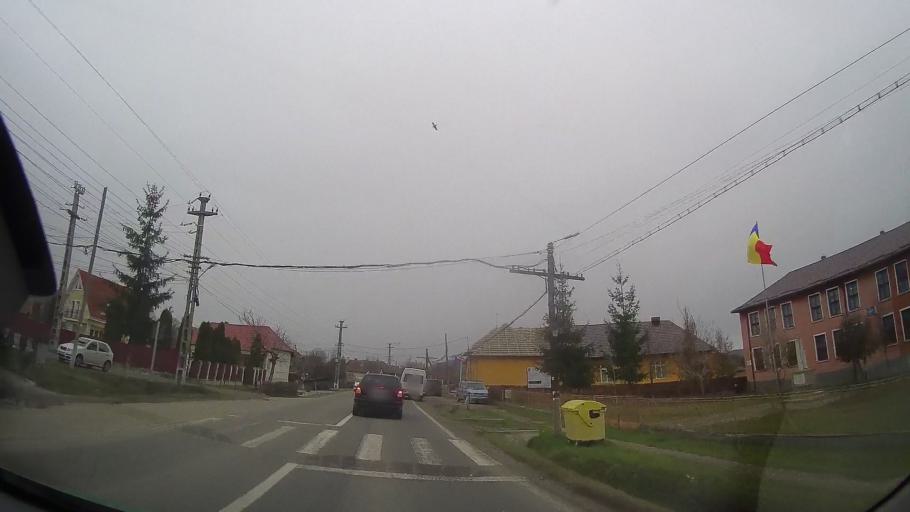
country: RO
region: Mures
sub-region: Comuna Ceausu de Campie
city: Ceausu de Campie
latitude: 46.6130
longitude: 24.5273
